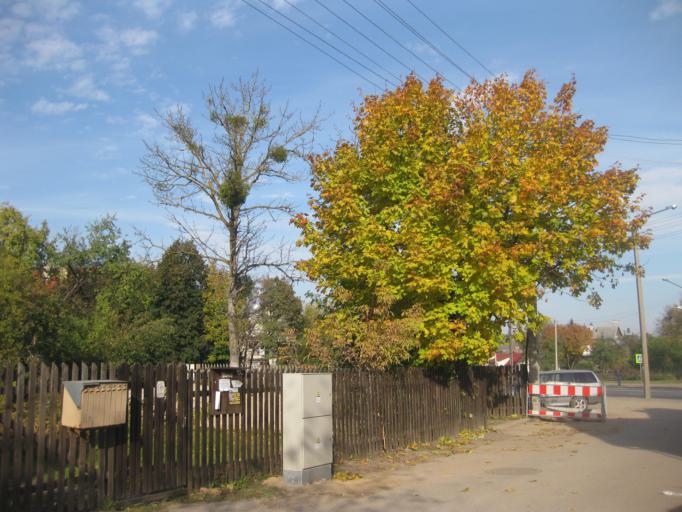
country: LT
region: Kauno apskritis
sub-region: Kaunas
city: Aleksotas
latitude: 54.8860
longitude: 23.8948
